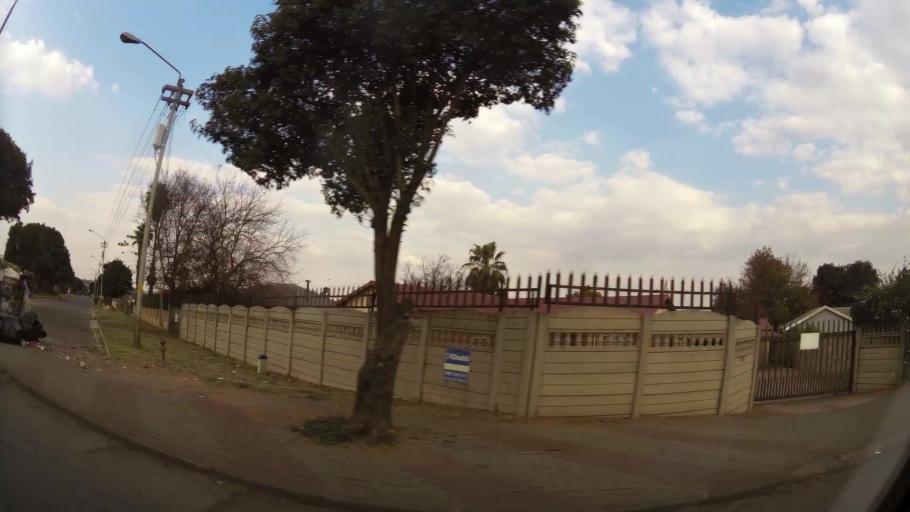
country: ZA
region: Gauteng
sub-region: Ekurhuleni Metropolitan Municipality
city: Germiston
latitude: -26.2450
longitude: 28.1900
